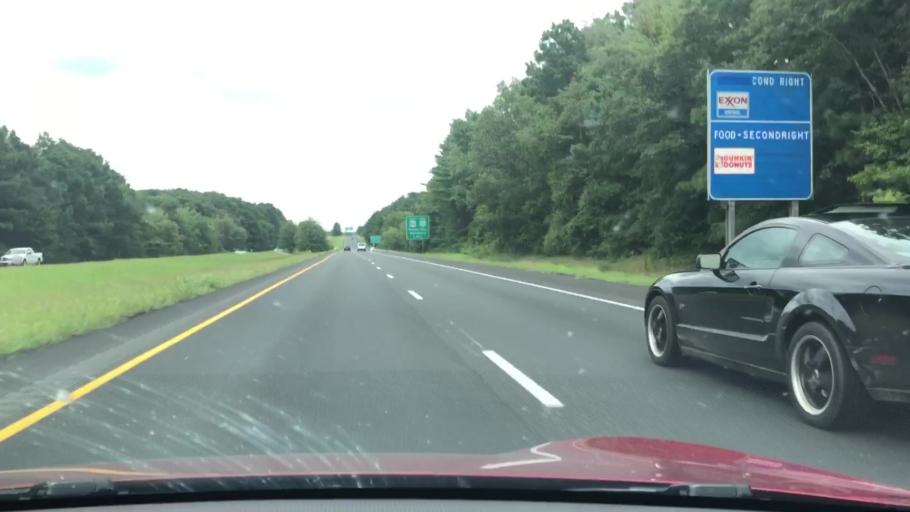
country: US
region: Maryland
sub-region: Wicomico County
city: Salisbury
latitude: 38.3490
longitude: -75.5429
